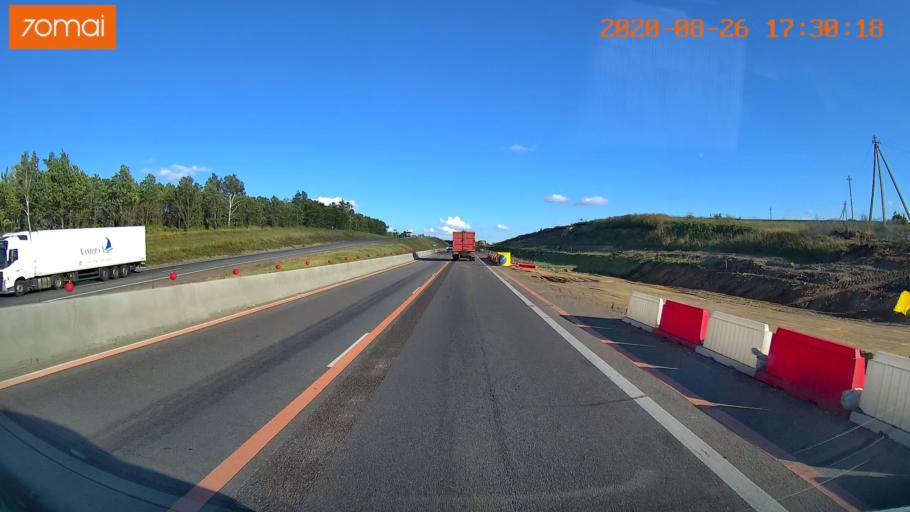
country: RU
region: Tula
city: Kazachka
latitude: 53.4461
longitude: 38.1667
